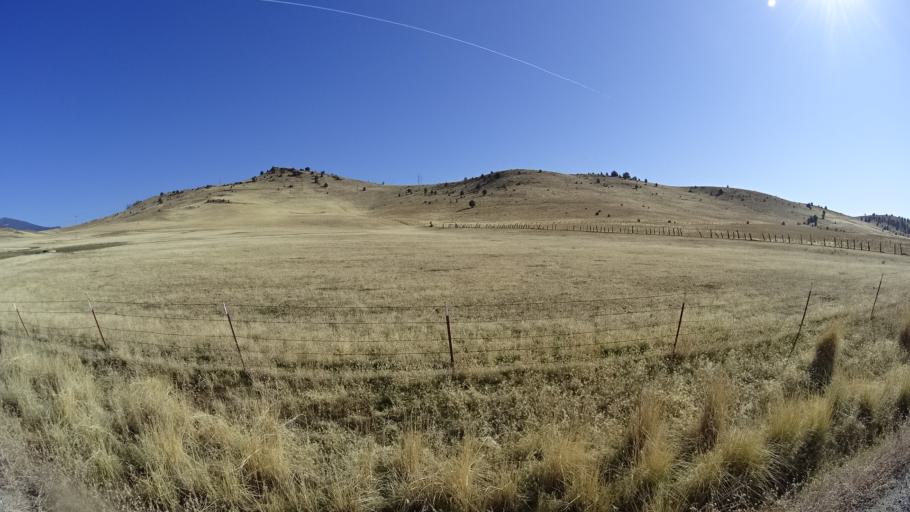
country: US
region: California
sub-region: Siskiyou County
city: Montague
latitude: 41.7422
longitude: -122.3663
